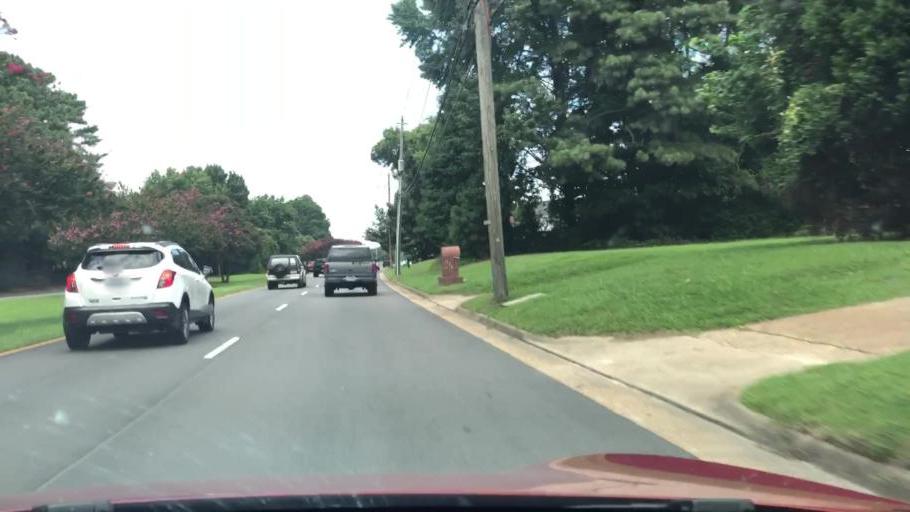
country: US
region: Virginia
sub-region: City of Norfolk
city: Norfolk
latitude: 36.8885
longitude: -76.1371
